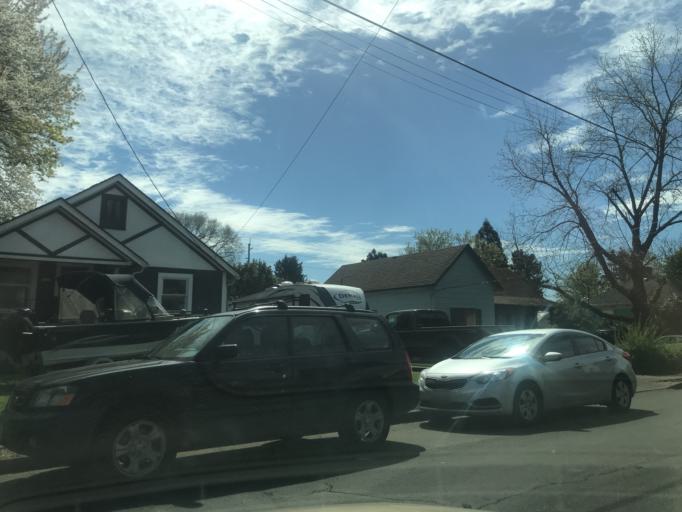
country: US
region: Oregon
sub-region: Multnomah County
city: Lents
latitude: 45.4855
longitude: -122.5958
